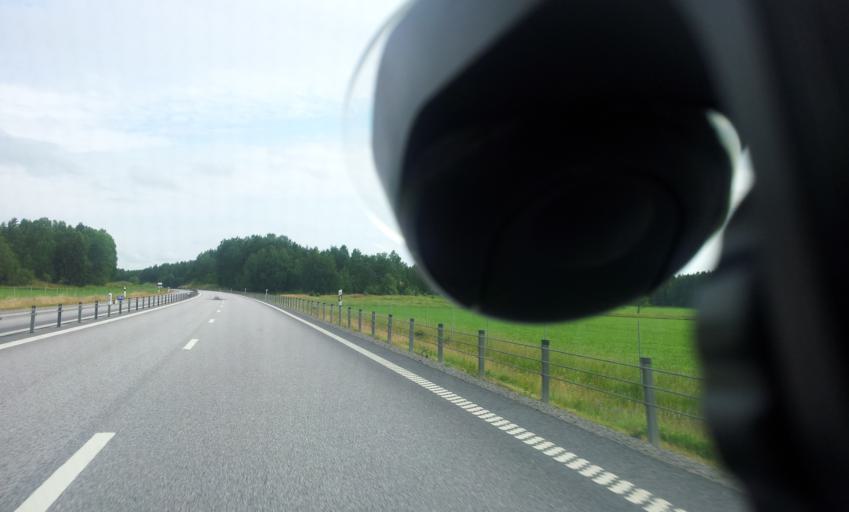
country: SE
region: OEstergoetland
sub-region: Soderkopings Kommun
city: Soederkoeping
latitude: 58.4116
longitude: 16.4012
